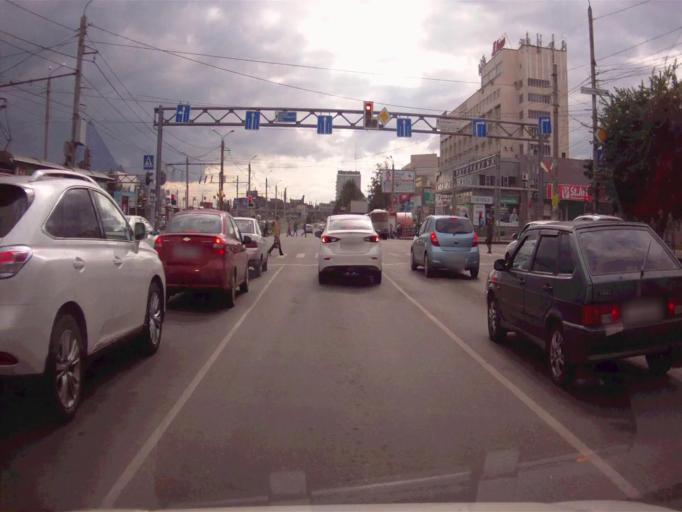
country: RU
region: Chelyabinsk
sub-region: Gorod Chelyabinsk
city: Chelyabinsk
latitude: 55.1425
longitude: 61.4131
